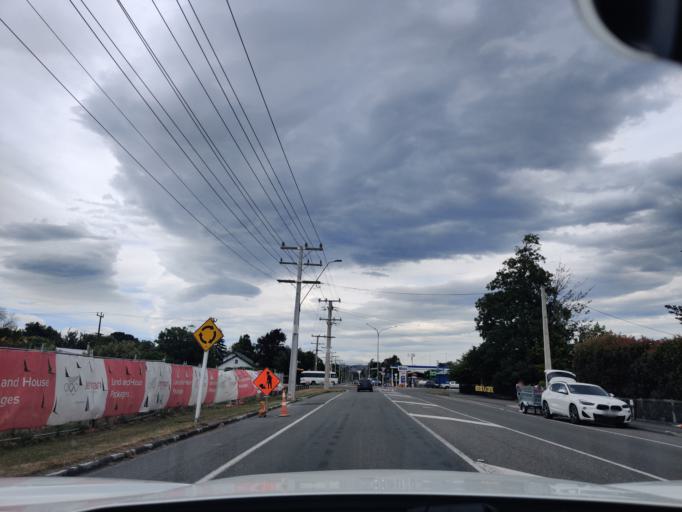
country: NZ
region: Wellington
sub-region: Masterton District
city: Masterton
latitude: -40.9470
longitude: 175.6364
